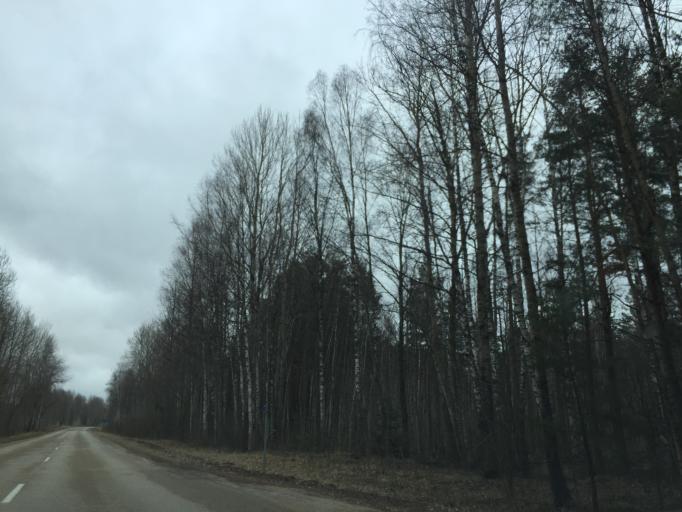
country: LV
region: Ilukste
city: Ilukste
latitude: 55.9641
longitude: 26.3038
